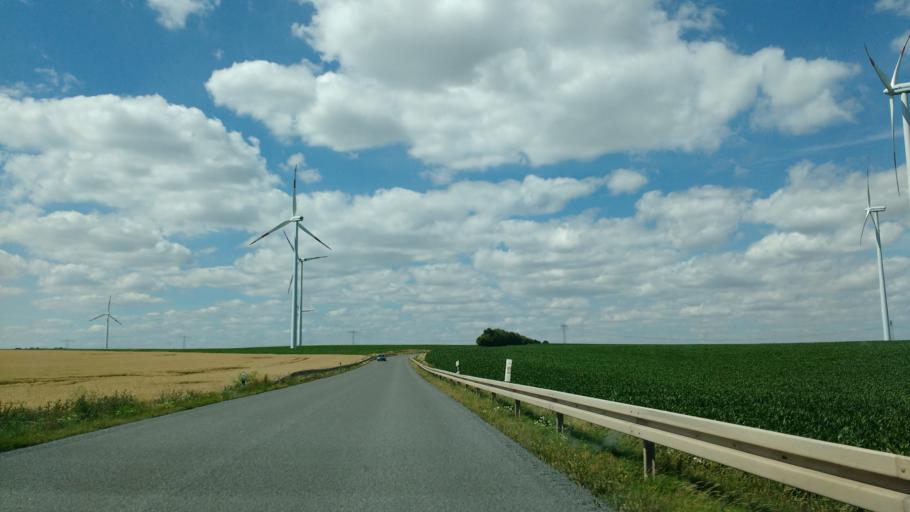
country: DE
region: Saxony-Anhalt
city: Farnstadt
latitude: 51.4075
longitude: 11.5824
